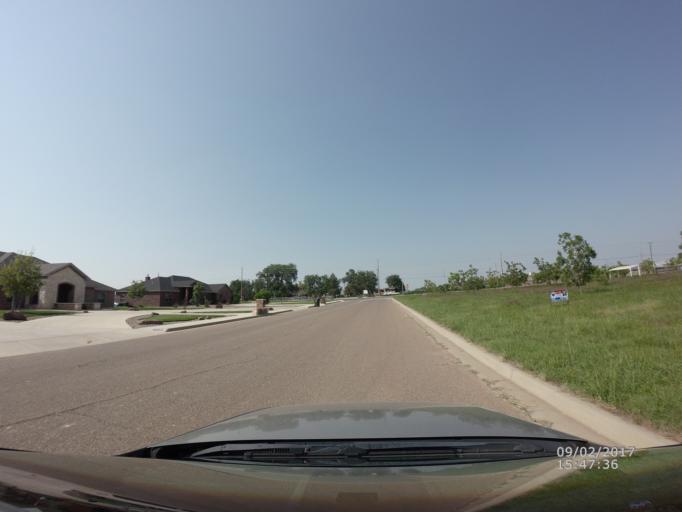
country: US
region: New Mexico
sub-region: Curry County
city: Clovis
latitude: 34.4475
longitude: -103.1911
